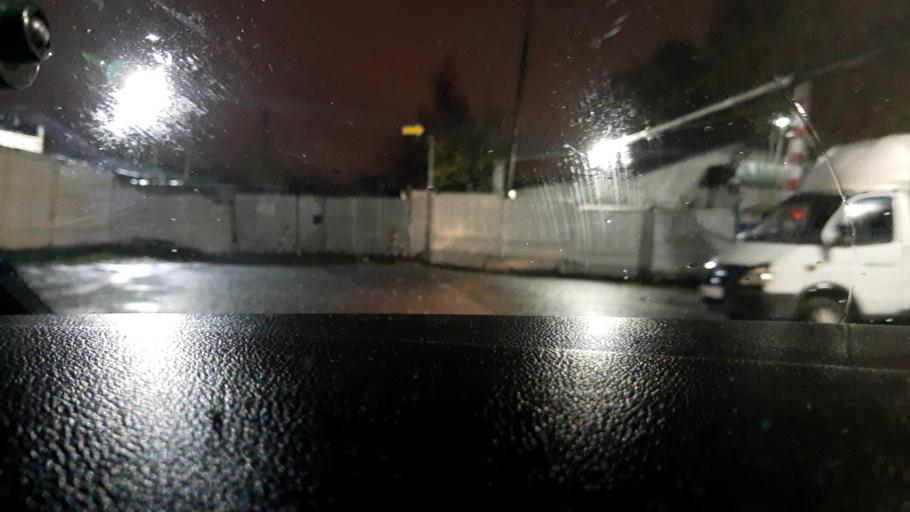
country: RU
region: Moskovskaya
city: Mosrentgen
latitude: 55.6075
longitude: 37.4653
